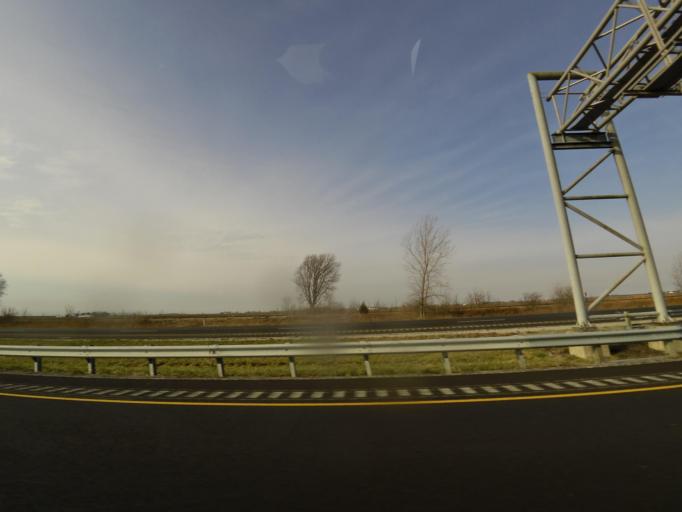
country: US
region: Illinois
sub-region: Macon County
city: Macon
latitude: 39.7576
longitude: -88.9850
